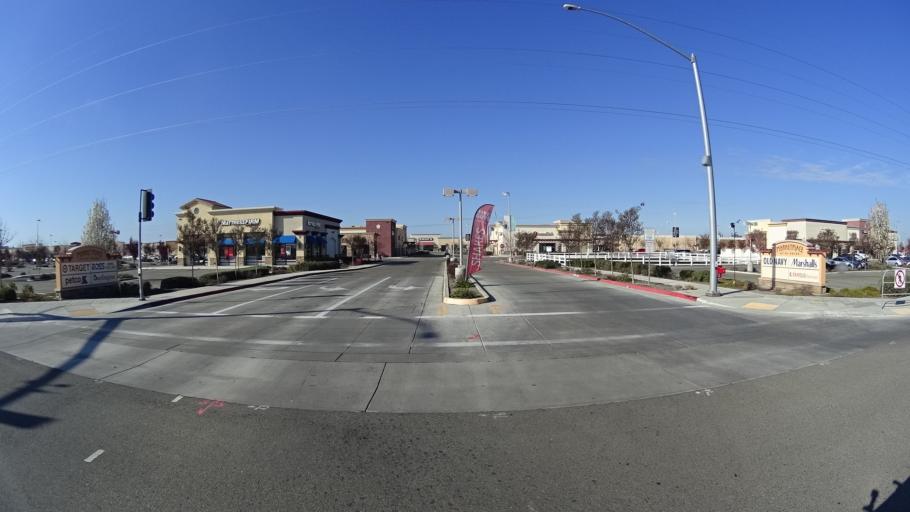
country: US
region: California
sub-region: Fresno County
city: Biola
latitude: 36.8343
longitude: -119.9091
